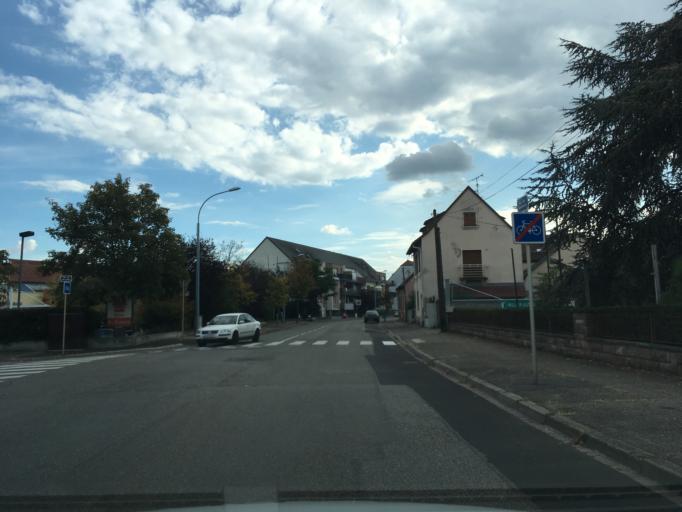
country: FR
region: Alsace
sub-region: Departement du Haut-Rhin
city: Colmar
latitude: 48.0887
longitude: 7.3578
